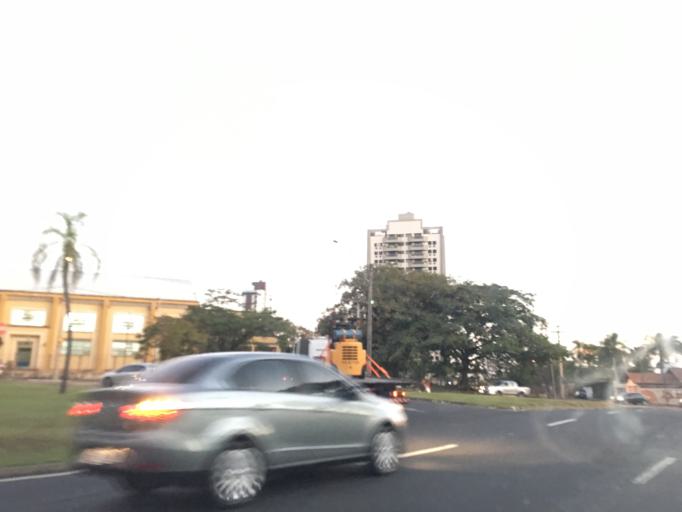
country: BR
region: Sao Paulo
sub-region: Piracicaba
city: Piracicaba
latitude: -22.7121
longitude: -47.6348
